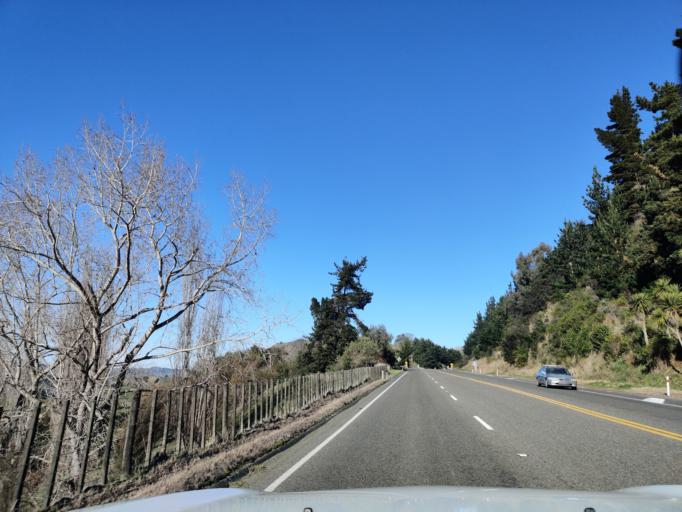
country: NZ
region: Manawatu-Wanganui
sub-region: Ruapehu District
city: Waiouru
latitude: -39.7664
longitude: 175.8009
